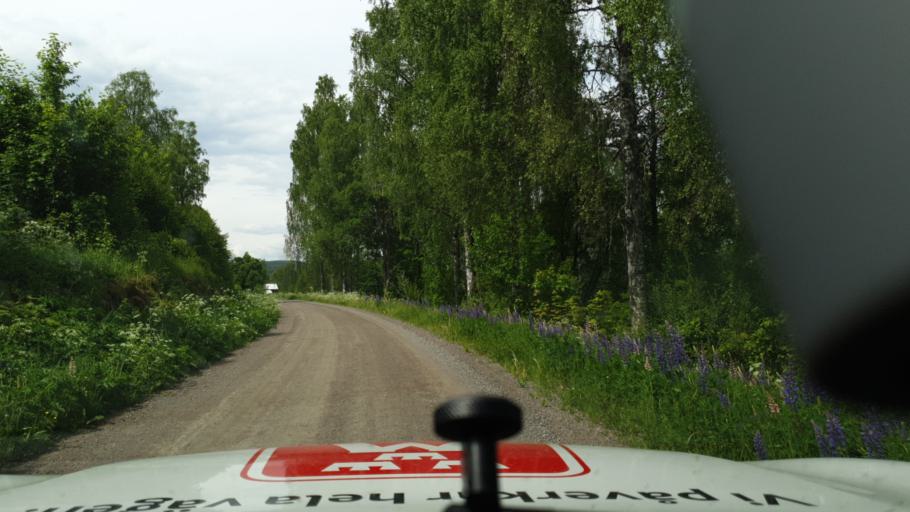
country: SE
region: Vaermland
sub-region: Torsby Kommun
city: Torsby
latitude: 59.9742
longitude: 12.8582
